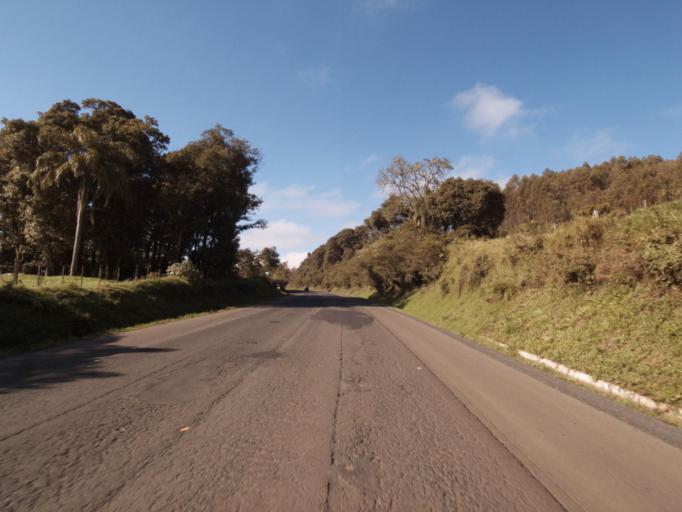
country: BR
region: Rio Grande do Sul
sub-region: Frederico Westphalen
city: Frederico Westphalen
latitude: -27.0569
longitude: -53.2274
